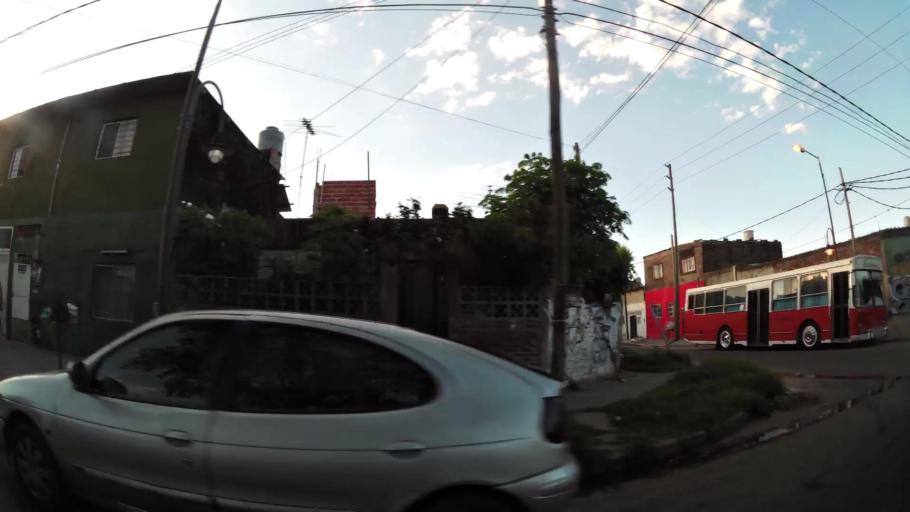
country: AR
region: Buenos Aires
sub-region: Partido de Tigre
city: Tigre
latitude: -34.4461
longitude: -58.5710
